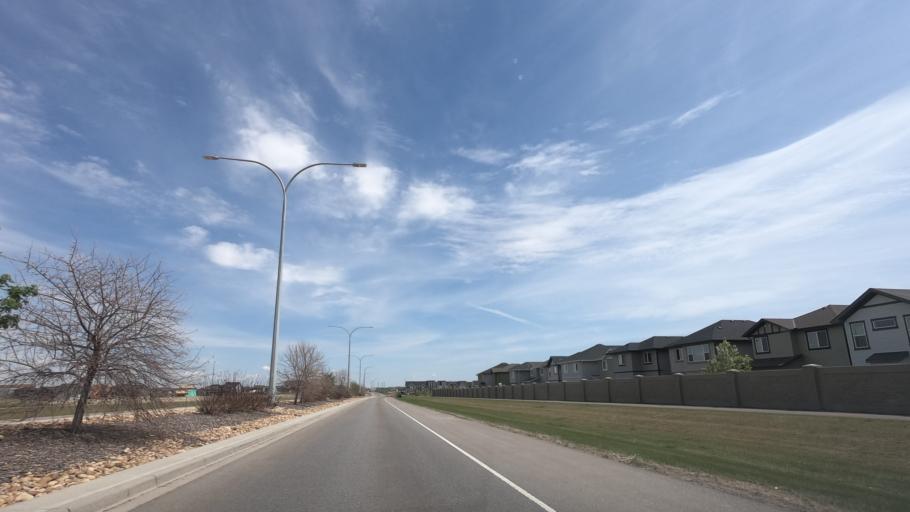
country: CA
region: Alberta
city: Airdrie
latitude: 51.2562
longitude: -114.0188
